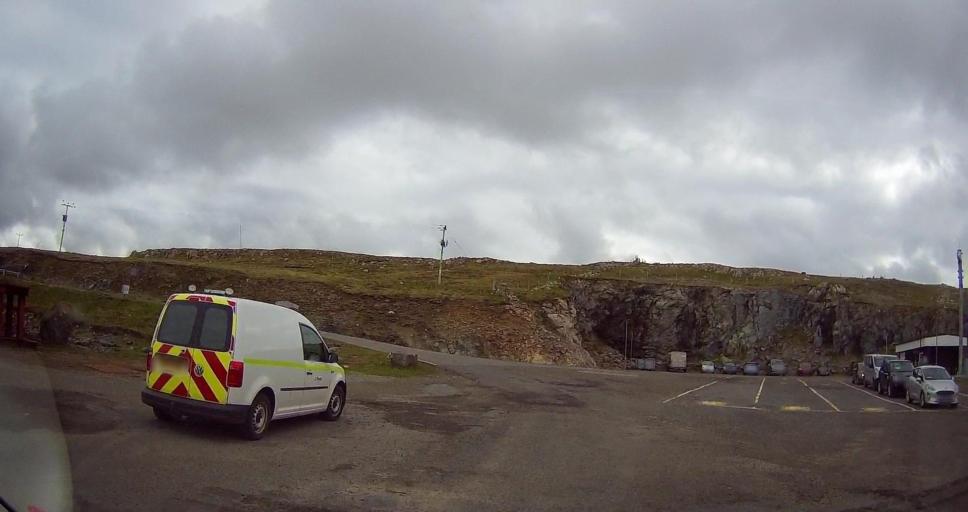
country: GB
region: Scotland
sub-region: Shetland Islands
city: Shetland
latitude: 60.6832
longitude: -0.9666
